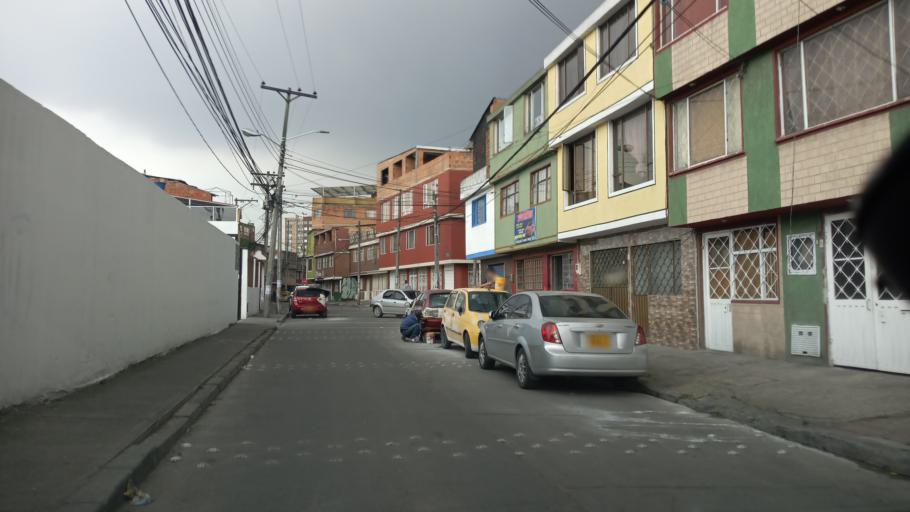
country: CO
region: Cundinamarca
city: Funza
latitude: 4.6709
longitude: -74.1499
